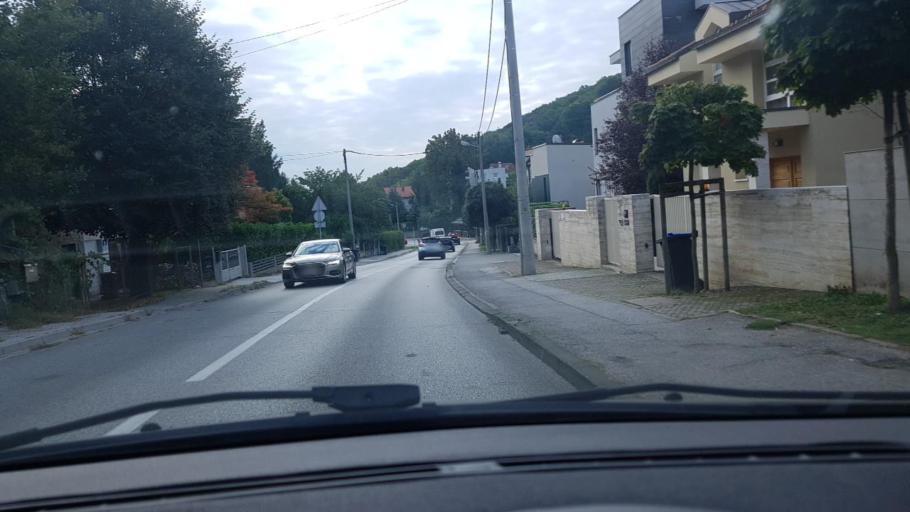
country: HR
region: Grad Zagreb
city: Zagreb
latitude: 45.8478
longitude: 15.9636
